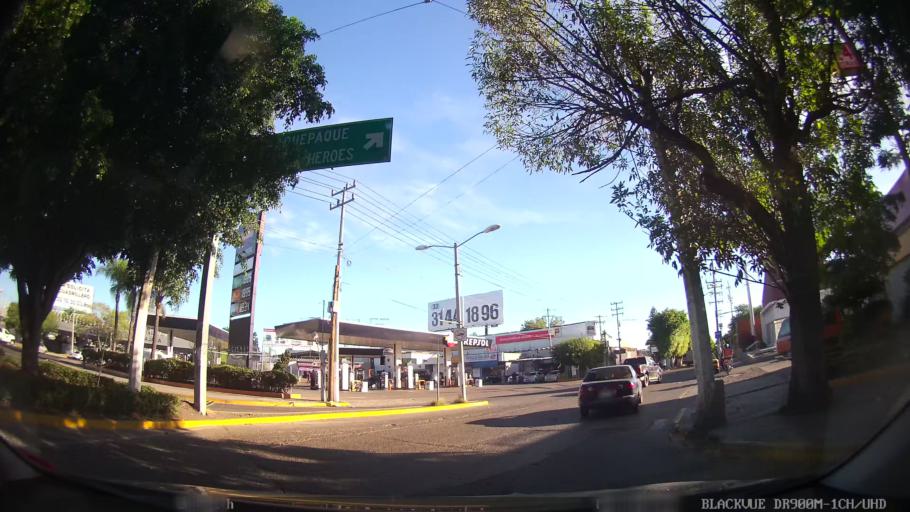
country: MX
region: Jalisco
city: Tlaquepaque
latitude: 20.6262
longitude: -103.3205
